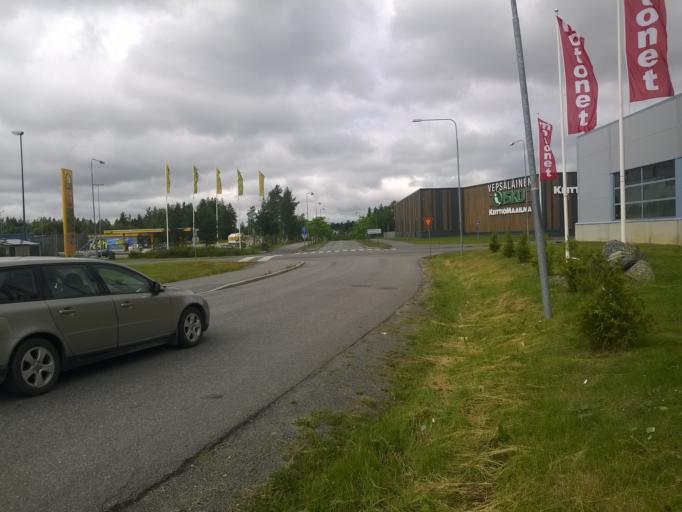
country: FI
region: Ostrobothnia
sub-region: Vaasa
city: Korsholm
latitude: 63.1113
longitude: 21.6550
